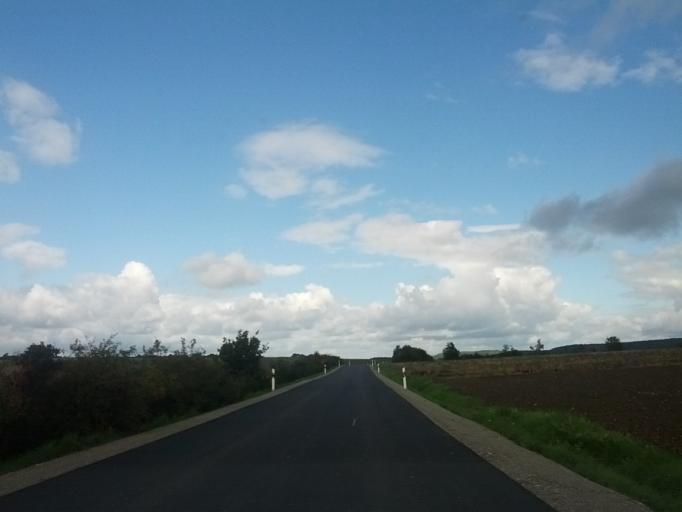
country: DE
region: Hesse
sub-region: Regierungsbezirk Kassel
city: Weissenborn
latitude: 51.0775
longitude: 10.0632
